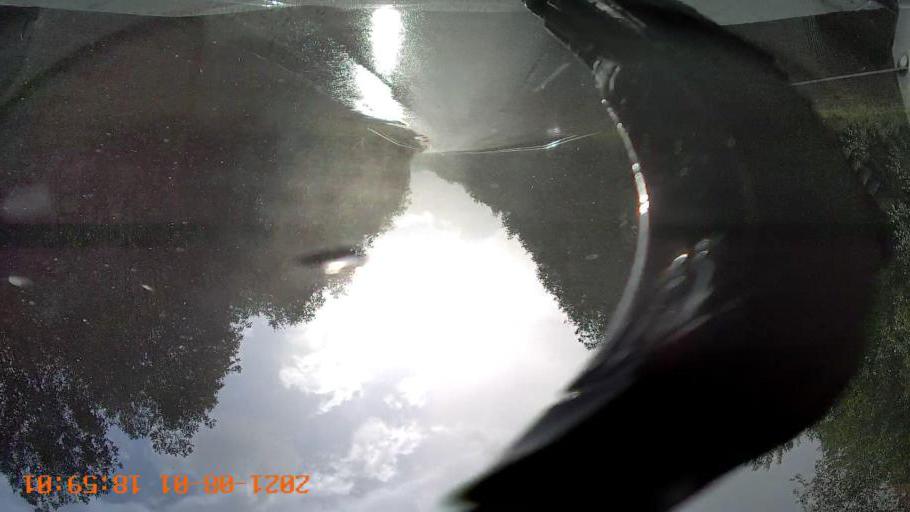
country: RU
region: Leningrad
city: Podporozh'ye
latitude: 60.9003
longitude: 34.6733
